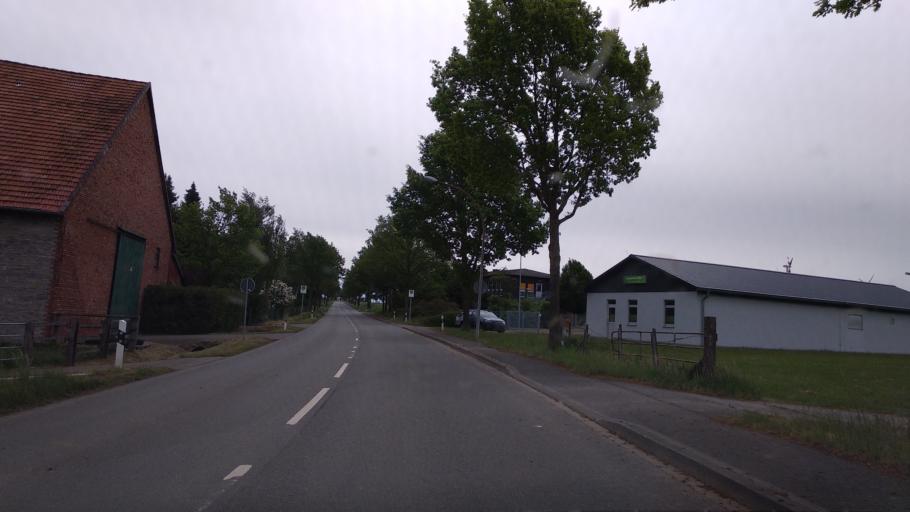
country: DE
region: North Rhine-Westphalia
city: Warburg
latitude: 51.5927
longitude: 9.1371
